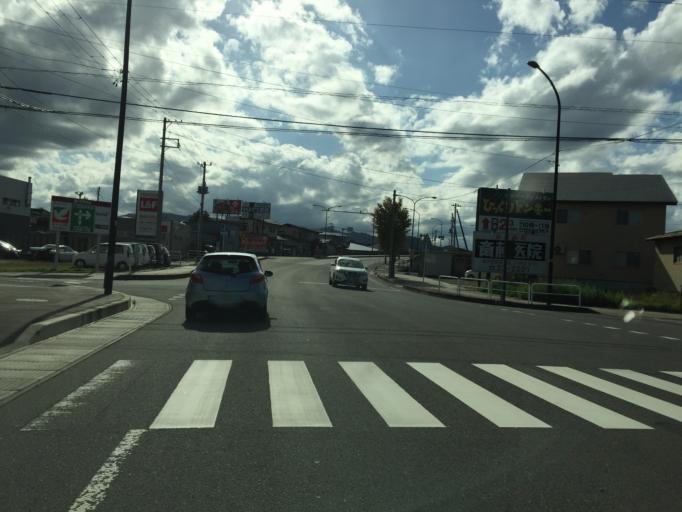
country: JP
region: Yamagata
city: Yonezawa
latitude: 37.9199
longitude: 140.1292
